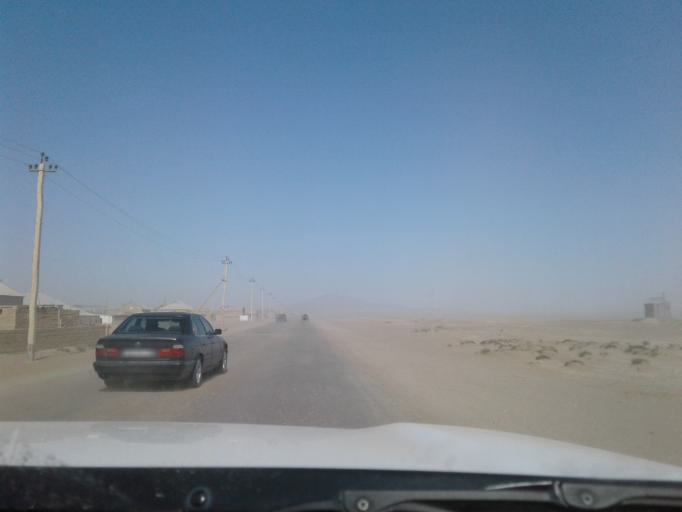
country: TM
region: Balkan
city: Gumdag
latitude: 39.1931
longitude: 54.5891
